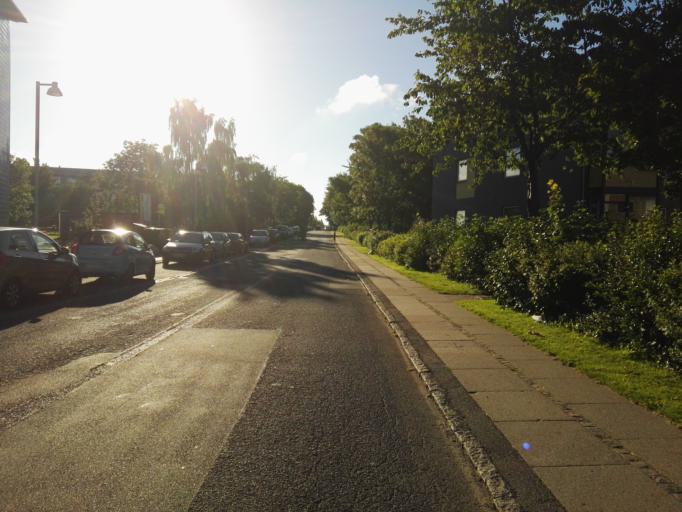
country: DK
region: Capital Region
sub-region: Ballerup Kommune
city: Ballerup
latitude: 55.7265
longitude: 12.3624
